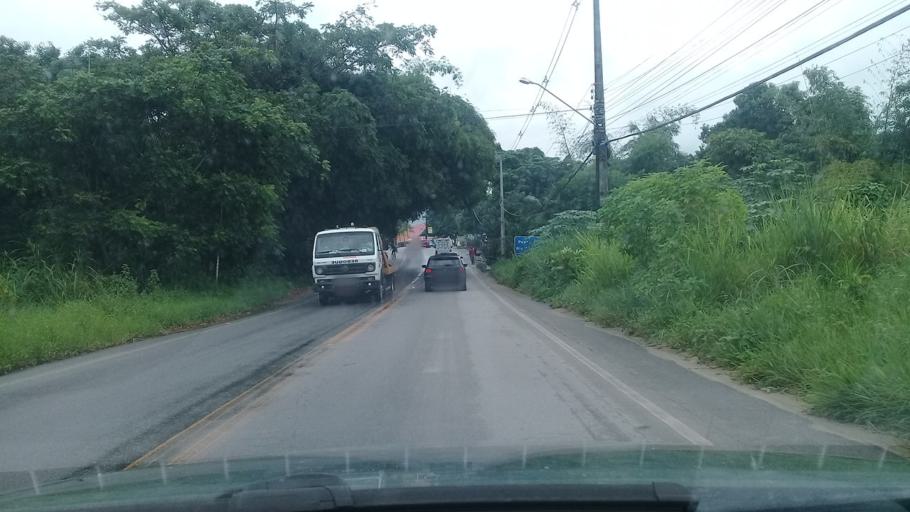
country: BR
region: Pernambuco
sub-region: Igarassu
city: Igarassu
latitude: -7.8191
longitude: -34.9113
